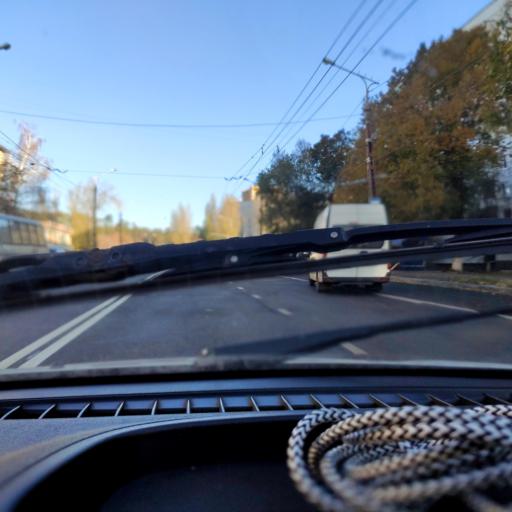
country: RU
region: Samara
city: Zhigulevsk
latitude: 53.4816
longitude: 49.4599
